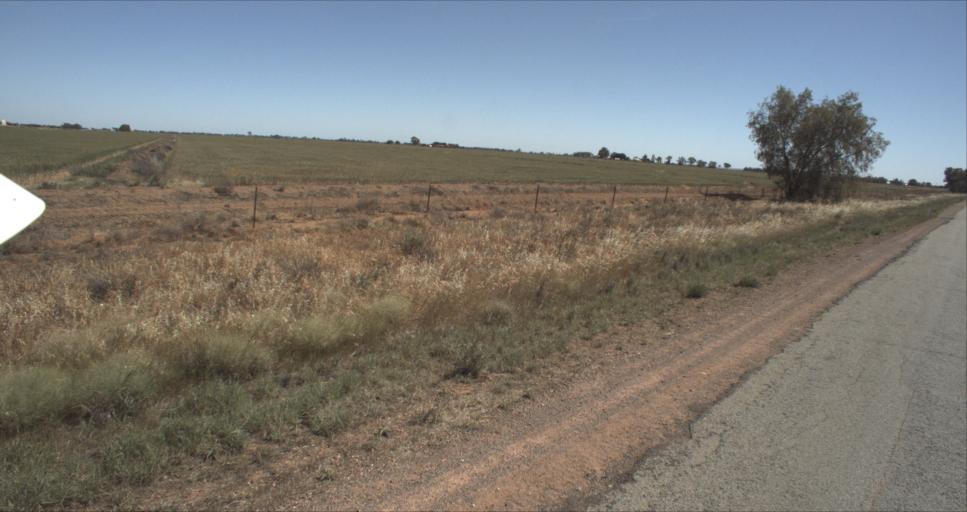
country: AU
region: New South Wales
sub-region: Leeton
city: Leeton
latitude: -34.5597
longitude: 146.3130
